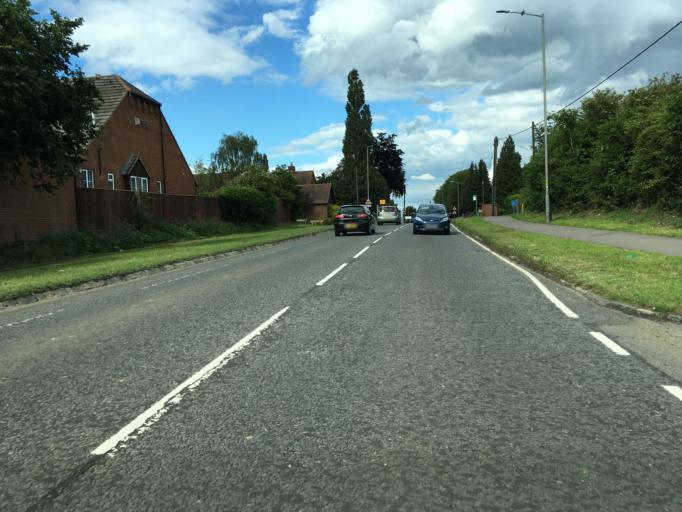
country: GB
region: England
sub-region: Buckinghamshire
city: Aylesbury
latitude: 51.8290
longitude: -0.7900
